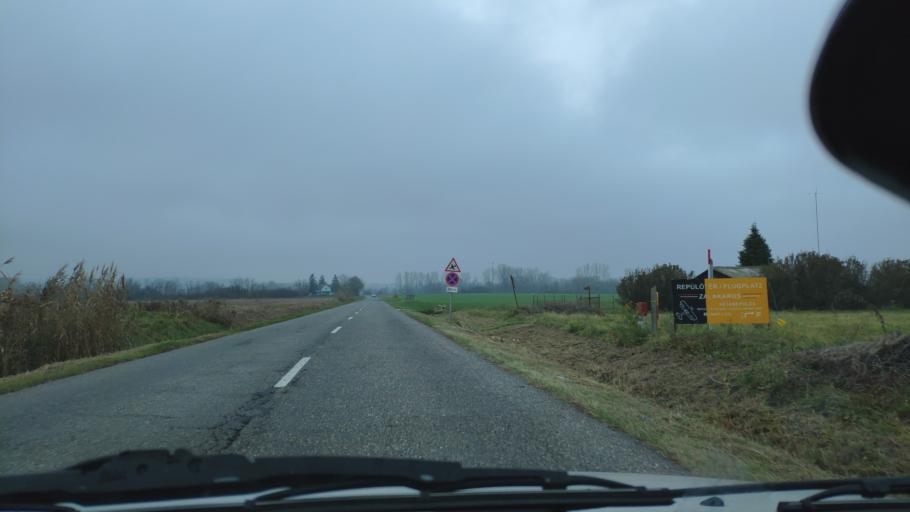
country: HU
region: Zala
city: Zalakomar
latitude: 46.5496
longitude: 17.1496
